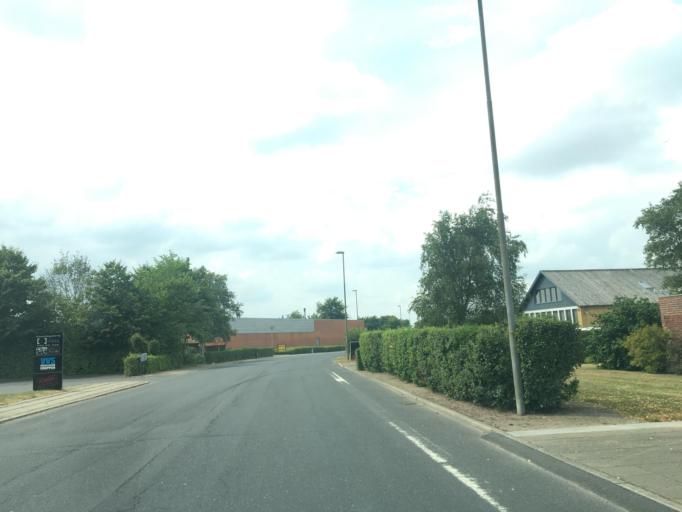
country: DK
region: Central Jutland
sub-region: Holstebro Kommune
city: Holstebro
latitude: 56.3637
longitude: 8.5960
